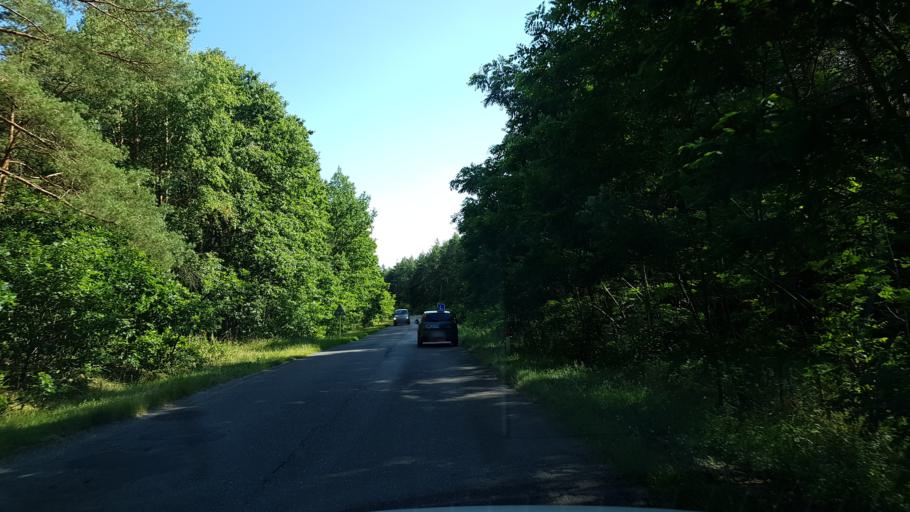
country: PL
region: West Pomeranian Voivodeship
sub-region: Powiat goleniowski
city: Stepnica
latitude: 53.7102
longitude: 14.6673
